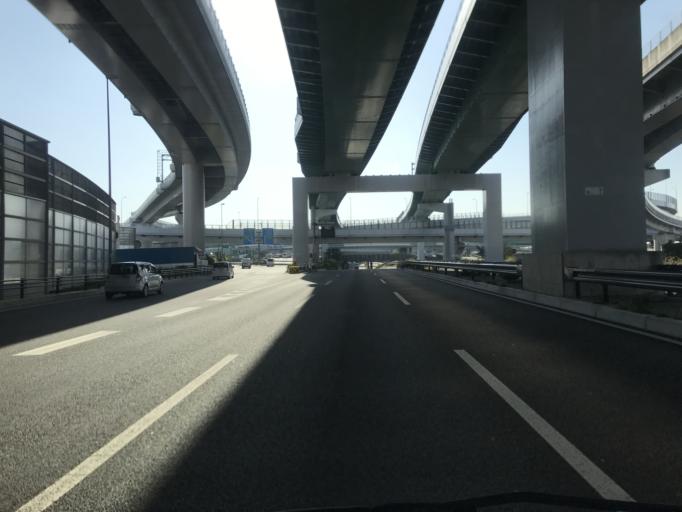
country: JP
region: Aichi
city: Iwakura
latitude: 35.2240
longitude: 136.8541
